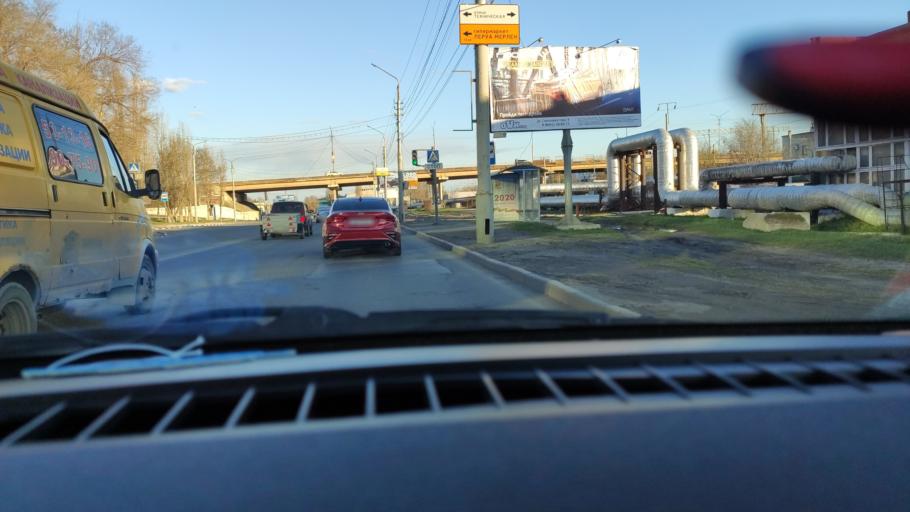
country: RU
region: Saratov
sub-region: Saratovskiy Rayon
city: Saratov
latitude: 51.5669
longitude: 45.9992
